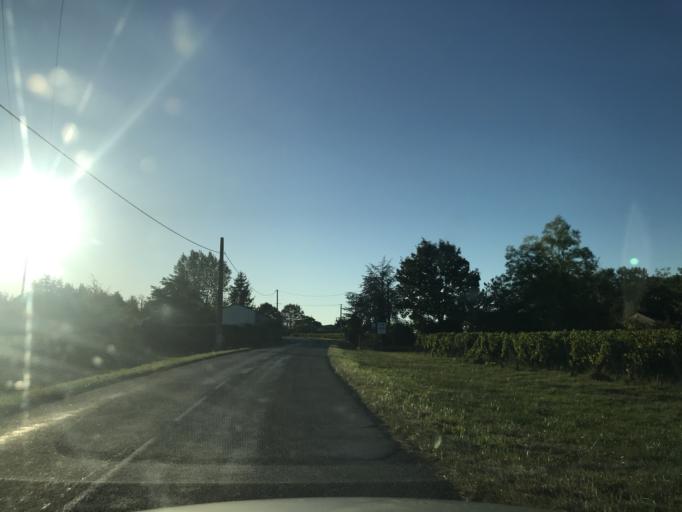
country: FR
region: Aquitaine
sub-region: Departement de la Gironde
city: Lussac
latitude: 44.8947
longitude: -0.0546
